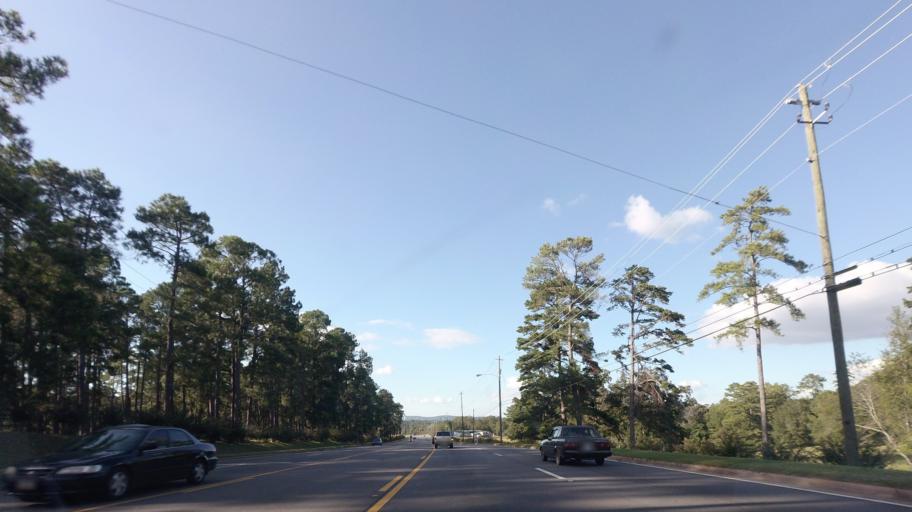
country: US
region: Georgia
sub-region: Upson County
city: Thomaston
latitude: 32.9063
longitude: -84.3296
